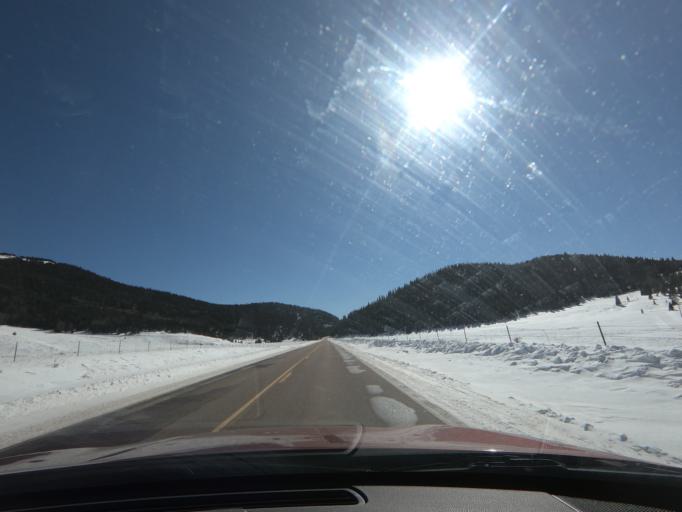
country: US
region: Colorado
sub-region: Teller County
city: Cripple Creek
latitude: 38.7582
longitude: -105.1085
